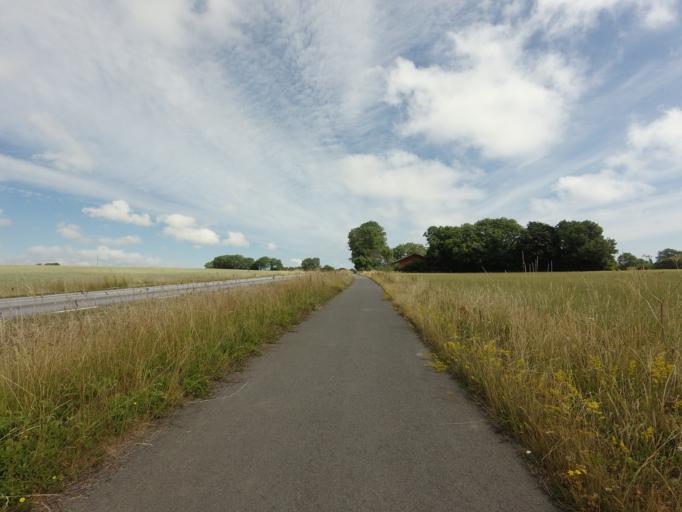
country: SE
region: Skane
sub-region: Simrishamns Kommun
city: Simrishamn
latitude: 55.5068
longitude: 14.3333
